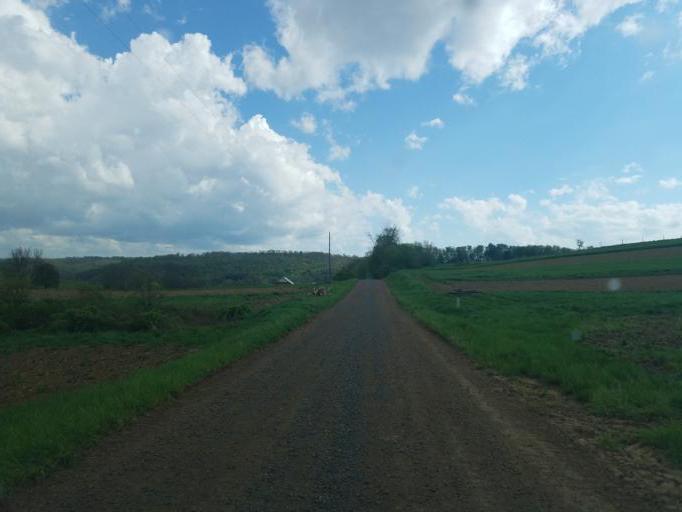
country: US
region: Ohio
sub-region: Knox County
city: Oak Hill
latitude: 40.4202
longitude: -82.2127
